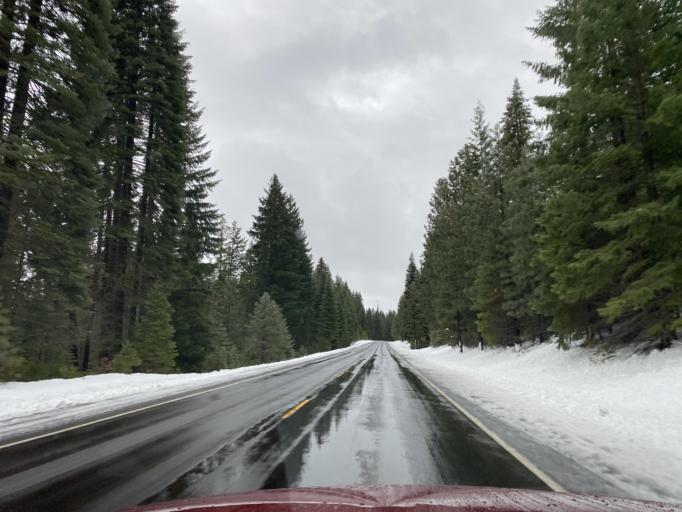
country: US
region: Oregon
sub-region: Klamath County
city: Klamath Falls
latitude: 42.5072
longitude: -122.0831
